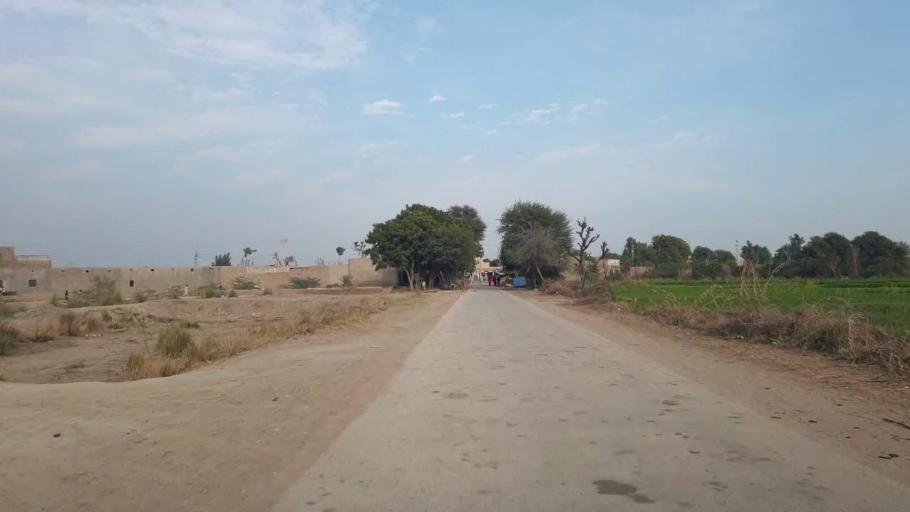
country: PK
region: Sindh
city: Shahpur Chakar
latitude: 26.0565
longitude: 68.5749
